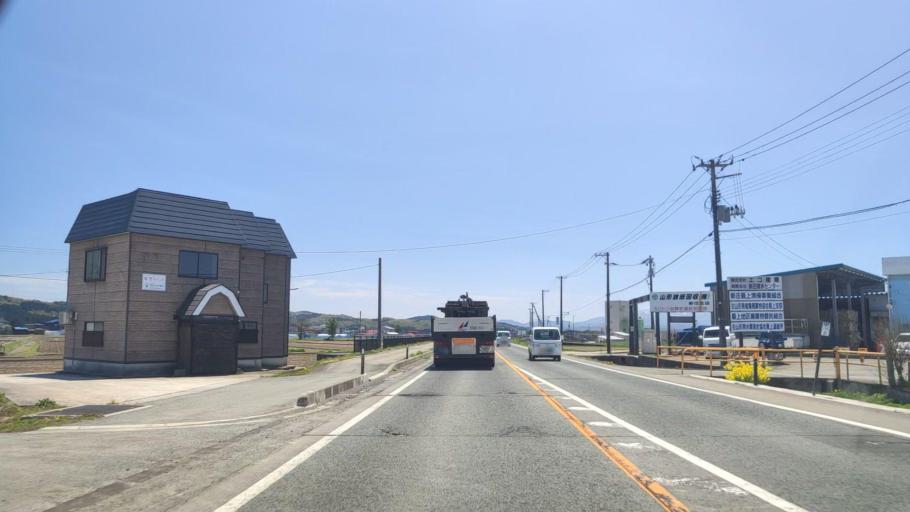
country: JP
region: Yamagata
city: Shinjo
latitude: 38.7937
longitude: 140.3185
